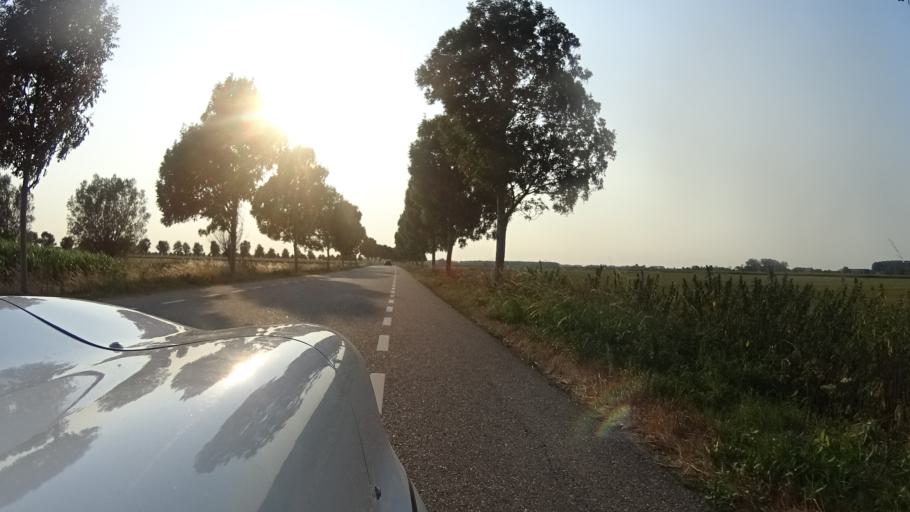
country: NL
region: Gelderland
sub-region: Gemeente Druten
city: Druten
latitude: 51.8457
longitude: 5.5449
